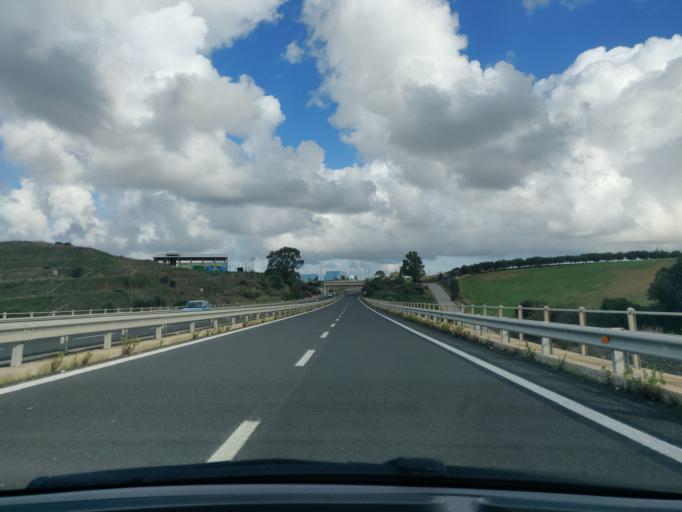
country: IT
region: Latium
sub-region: Citta metropolitana di Roma Capitale
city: Aurelia
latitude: 42.1172
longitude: 11.7918
